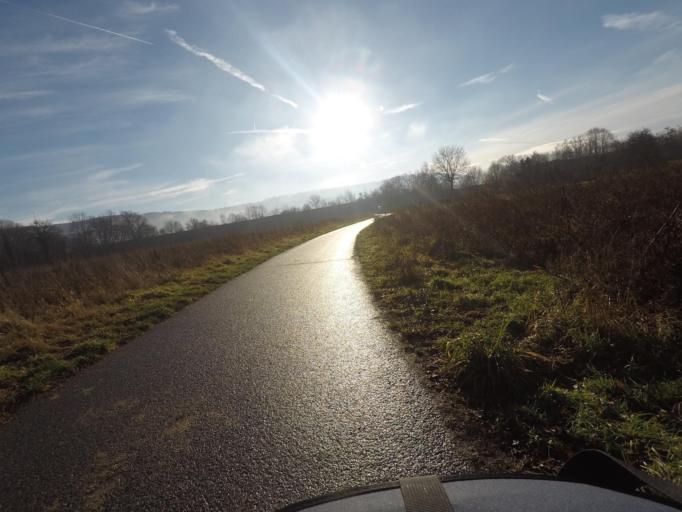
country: DE
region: Baden-Wuerttemberg
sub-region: Karlsruhe Region
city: Ettlingen
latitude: 48.9669
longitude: 8.4187
